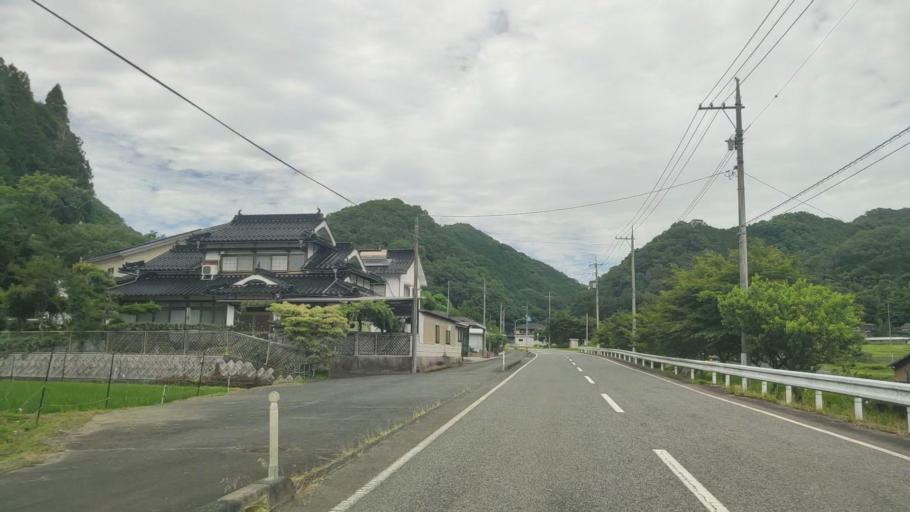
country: JP
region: Hyogo
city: Yamazakicho-nakabirose
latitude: 35.1030
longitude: 134.2974
